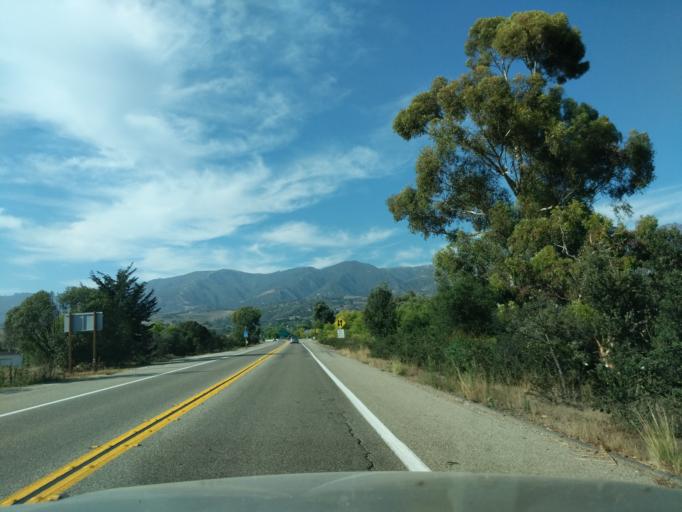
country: US
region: California
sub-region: Santa Barbara County
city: Mission Canyon
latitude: 34.4446
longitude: -119.7598
